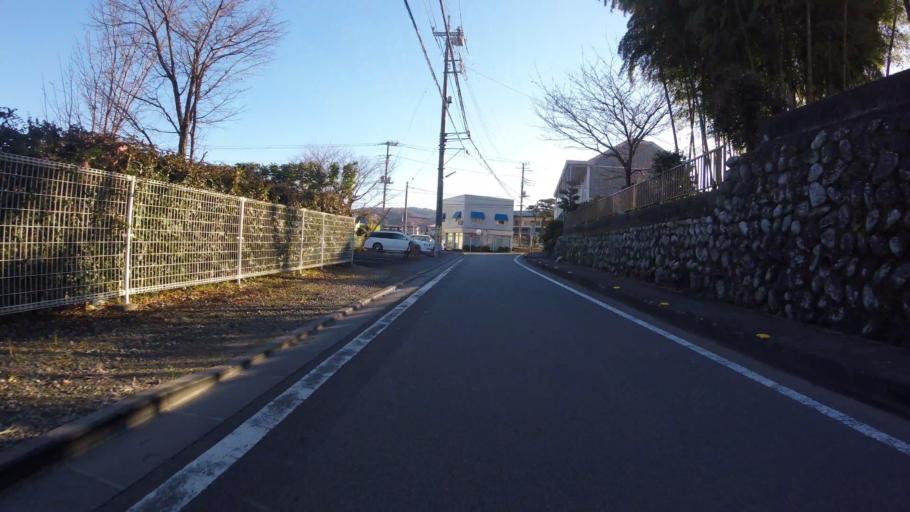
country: JP
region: Shizuoka
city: Mishima
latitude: 34.9893
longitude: 138.9430
